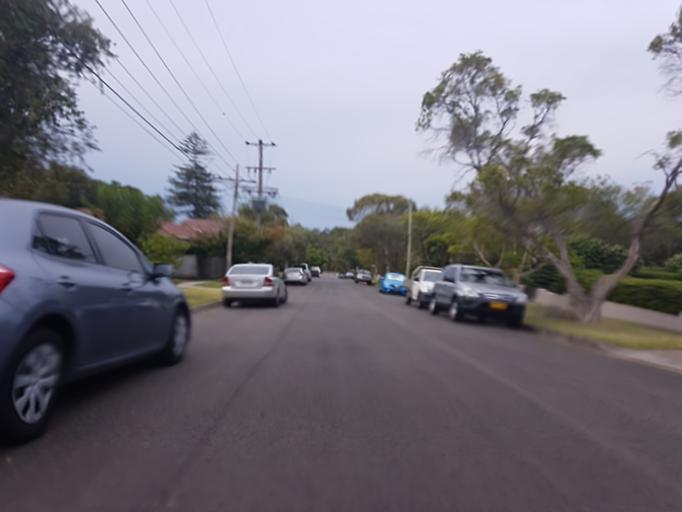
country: AU
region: New South Wales
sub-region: Ku-ring-gai
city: Roseville Chase
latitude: -33.7788
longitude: 151.1978
